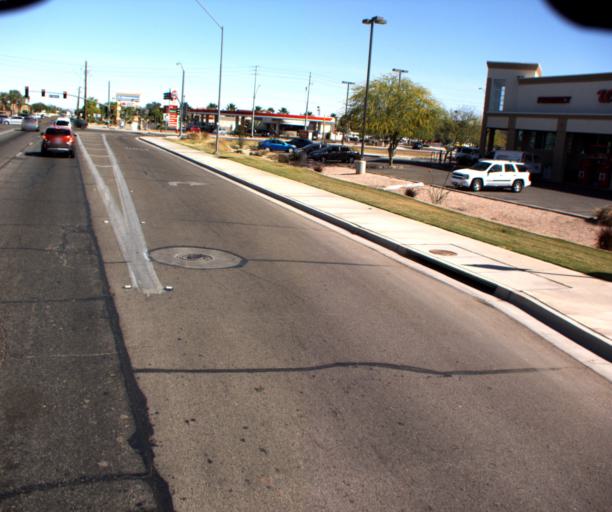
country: US
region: Arizona
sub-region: Yuma County
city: Yuma
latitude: 32.6829
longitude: -114.6503
